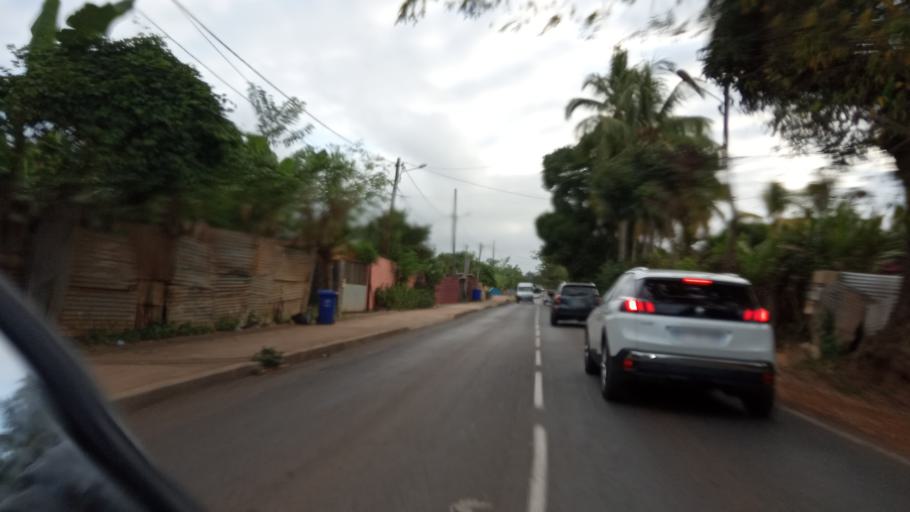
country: YT
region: Dembeni
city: Dembeni
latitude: -12.8133
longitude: 45.2018
